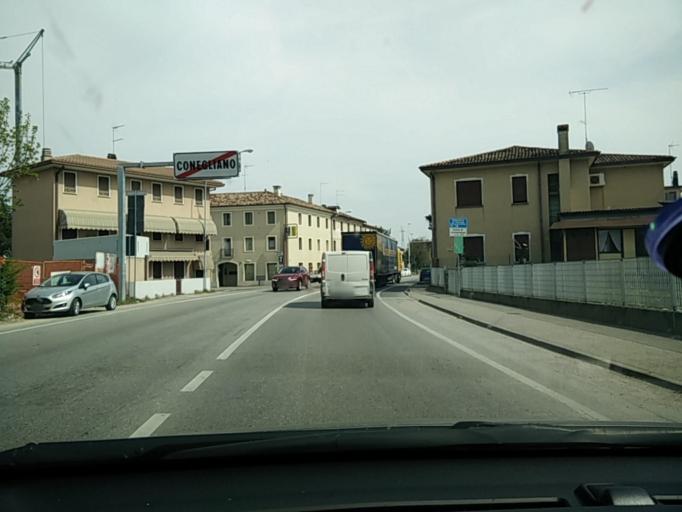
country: IT
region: Veneto
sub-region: Provincia di Treviso
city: San Vendemiano-Fossamerlo
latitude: 45.8833
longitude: 12.3180
